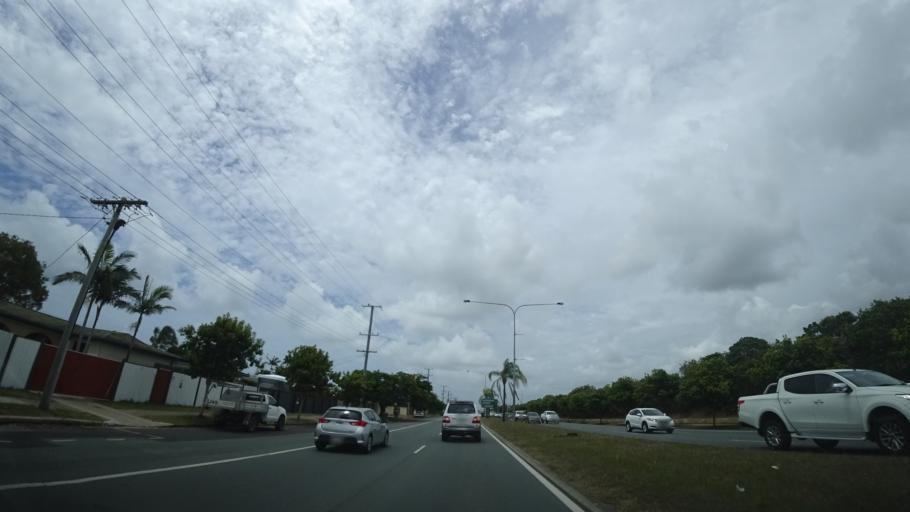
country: AU
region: Queensland
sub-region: Sunshine Coast
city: Mooloolaba
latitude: -26.7164
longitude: 153.1299
